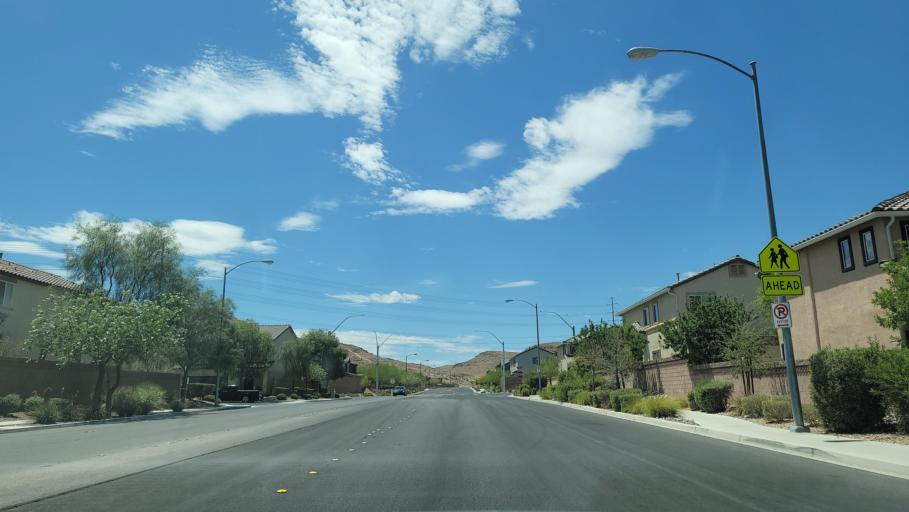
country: US
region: Nevada
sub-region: Clark County
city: Enterprise
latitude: 35.9924
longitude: -115.2346
